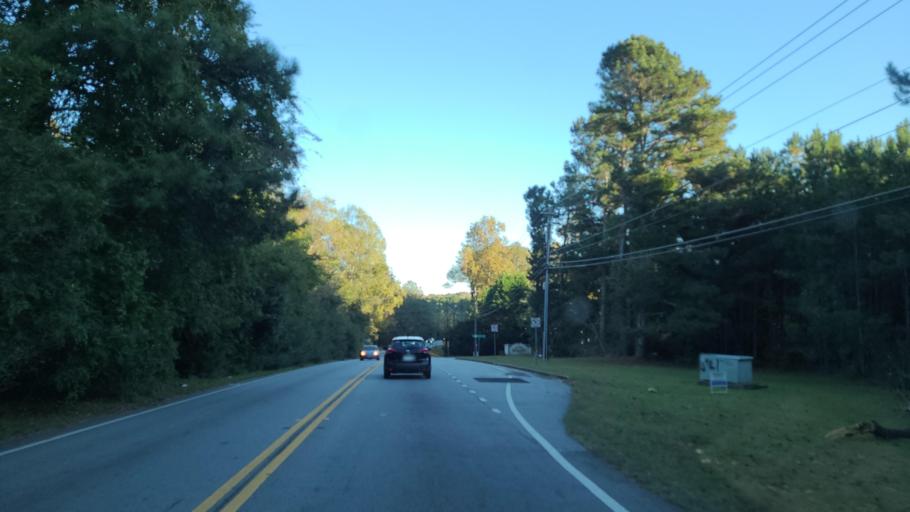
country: US
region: Georgia
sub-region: Henry County
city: Stockbridge
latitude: 33.5733
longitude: -84.2648
